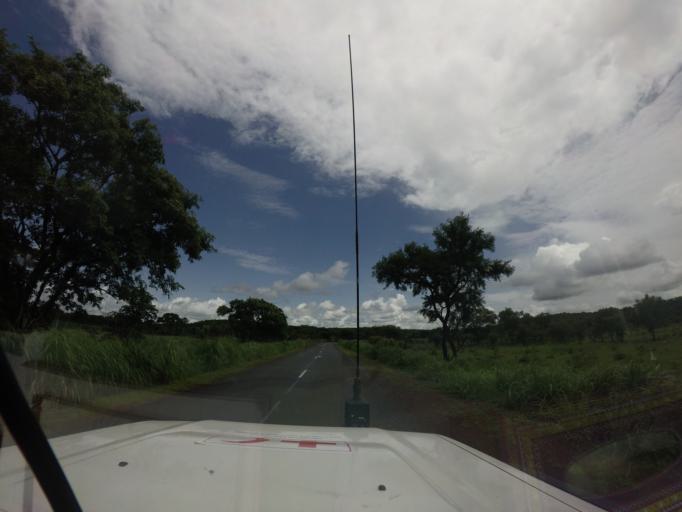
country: GN
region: Faranah
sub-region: Faranah Prefecture
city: Faranah
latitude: 10.0145
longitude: -10.9324
